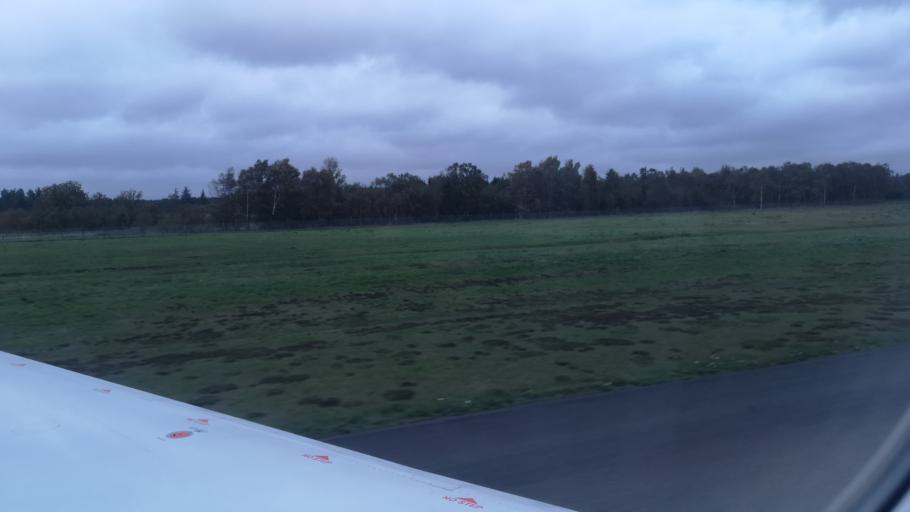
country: DK
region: South Denmark
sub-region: Billund Kommune
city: Billund
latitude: 55.7428
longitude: 9.1760
